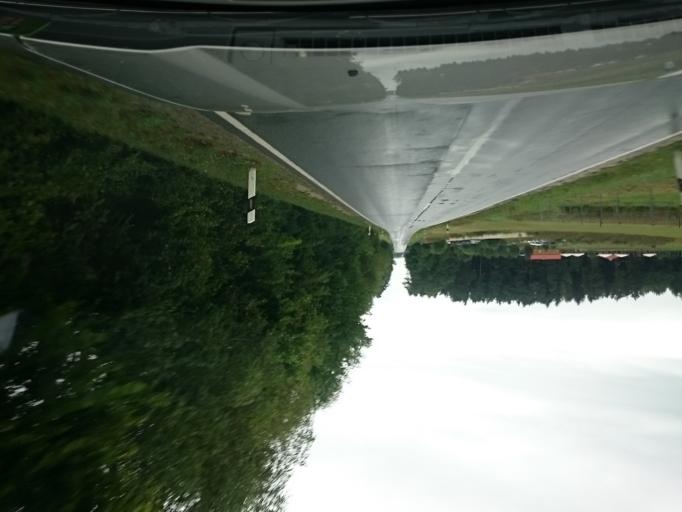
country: DE
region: Bavaria
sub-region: Upper Franconia
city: Pottenstein
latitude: 49.7530
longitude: 11.4041
